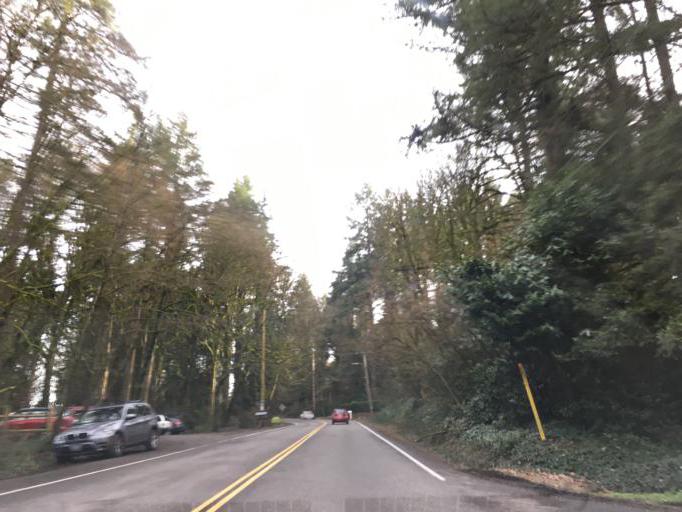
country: US
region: Oregon
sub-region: Clackamas County
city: Lake Oswego
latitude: 45.4428
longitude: -122.6867
